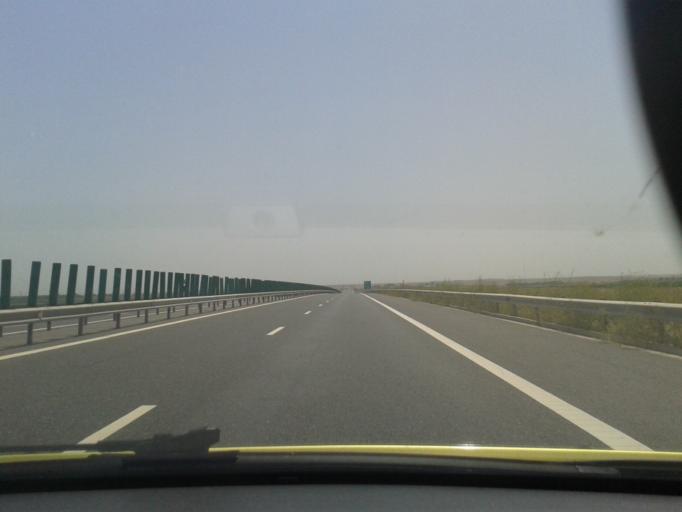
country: RO
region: Constanta
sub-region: Municipiul Constanta
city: Palazu Mare
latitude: 44.1927
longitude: 28.5513
